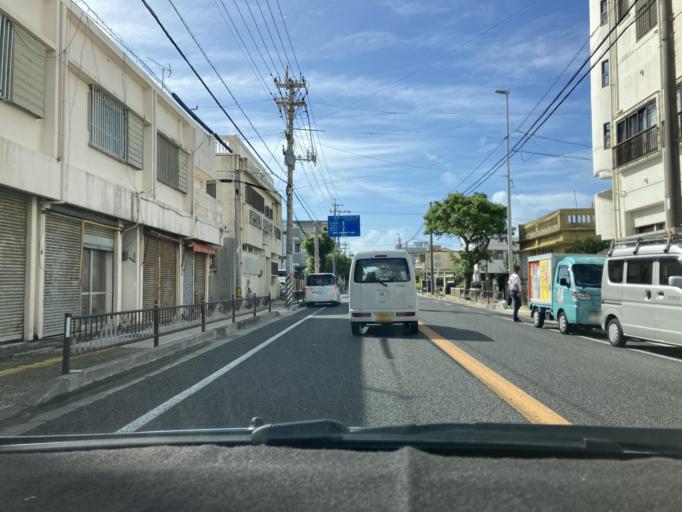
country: JP
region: Okinawa
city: Itoman
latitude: 26.1323
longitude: 127.6701
